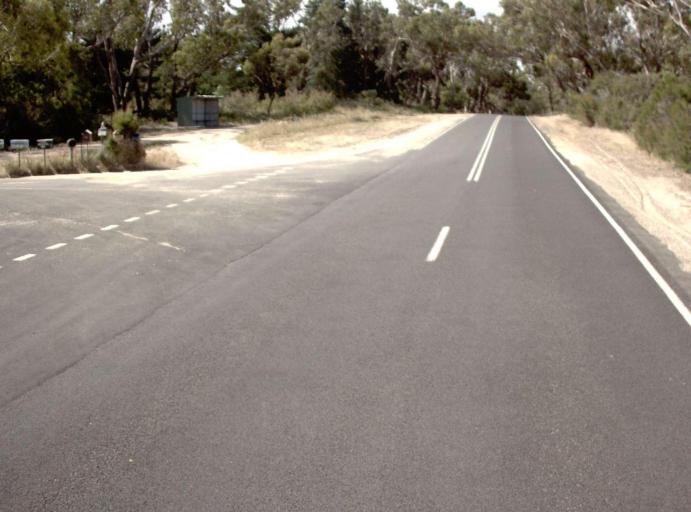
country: AU
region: Victoria
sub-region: Wellington
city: Sale
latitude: -38.2978
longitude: 147.1539
